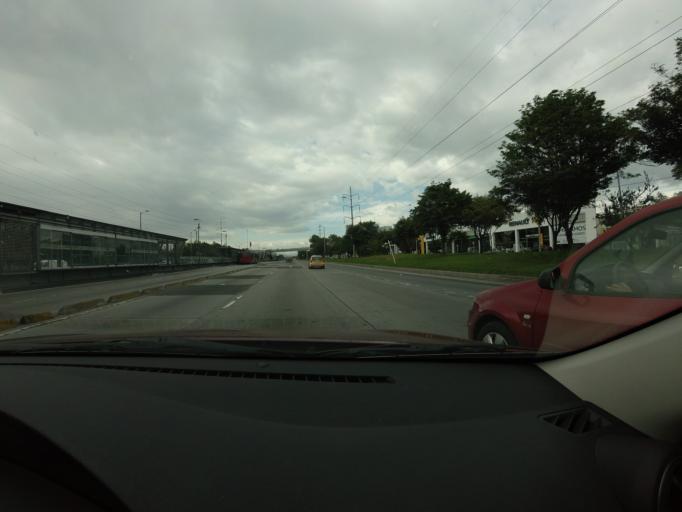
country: CO
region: Bogota D.C.
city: Barrio San Luis
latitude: 4.7404
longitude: -74.0481
